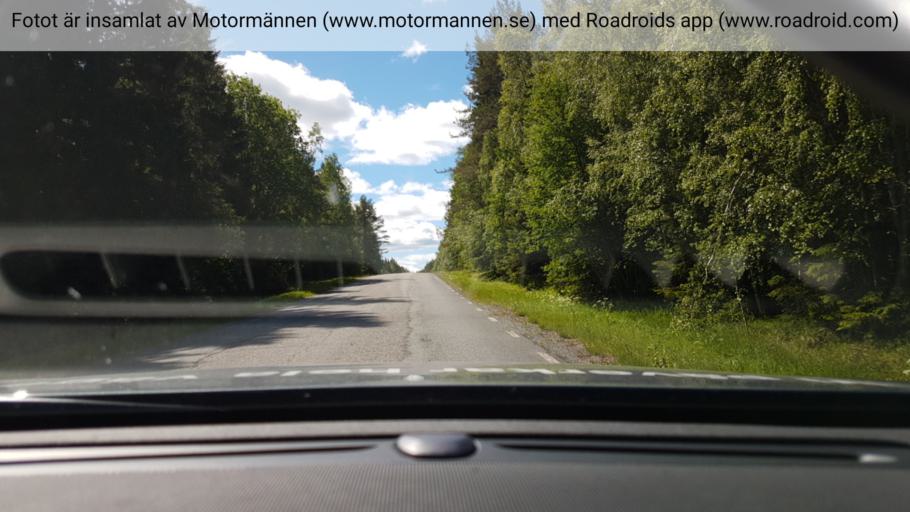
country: SE
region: Vaesterbotten
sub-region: Skelleftea Kommun
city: Burea
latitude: 64.4089
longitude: 21.3488
